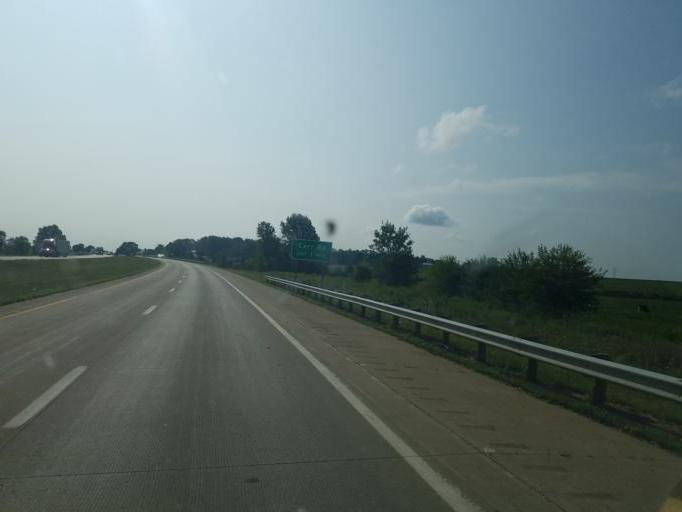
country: US
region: Ohio
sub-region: Wayne County
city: Apple Creek
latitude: 40.7943
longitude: -81.8096
